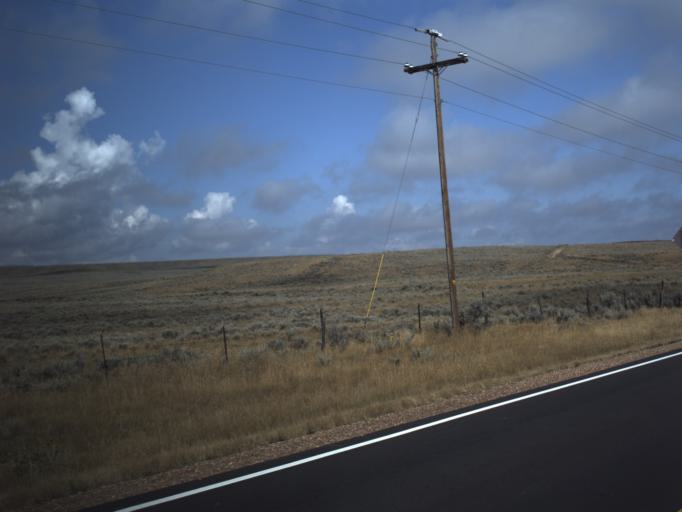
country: US
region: Utah
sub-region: Rich County
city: Randolph
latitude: 41.7338
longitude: -111.1588
